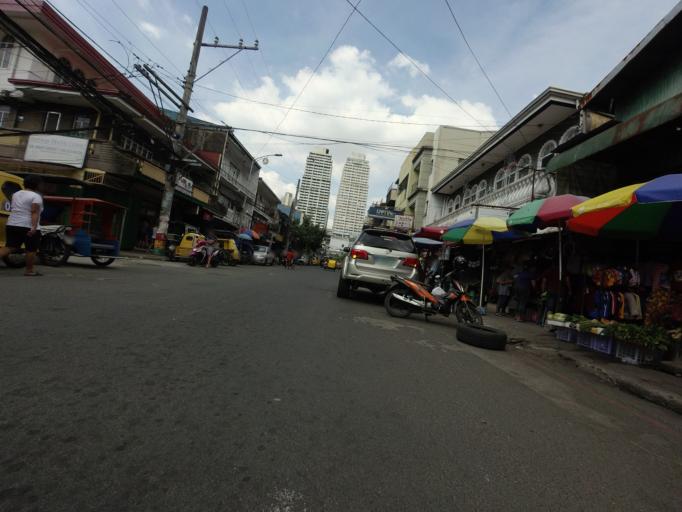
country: PH
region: Metro Manila
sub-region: City of Manila
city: Port Area
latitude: 14.5684
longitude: 120.9894
